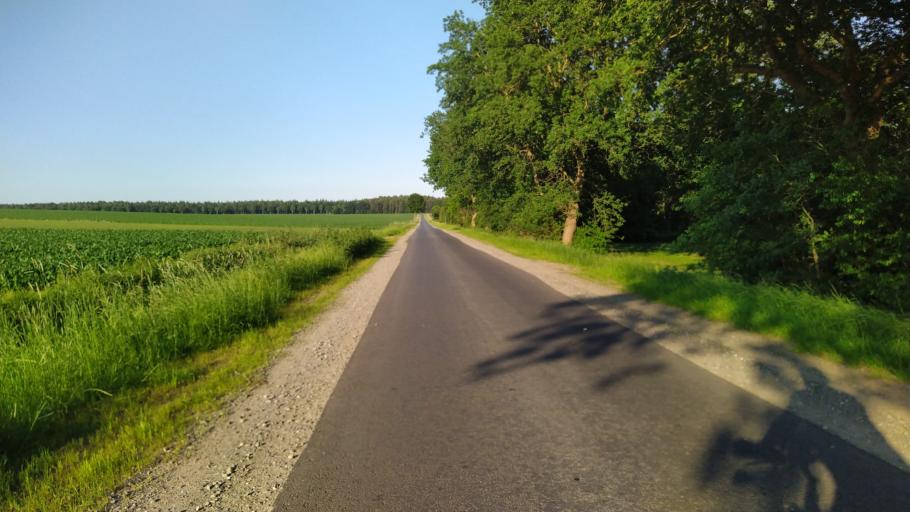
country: DE
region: Lower Saxony
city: Alfstedt
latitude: 53.5699
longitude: 9.0148
